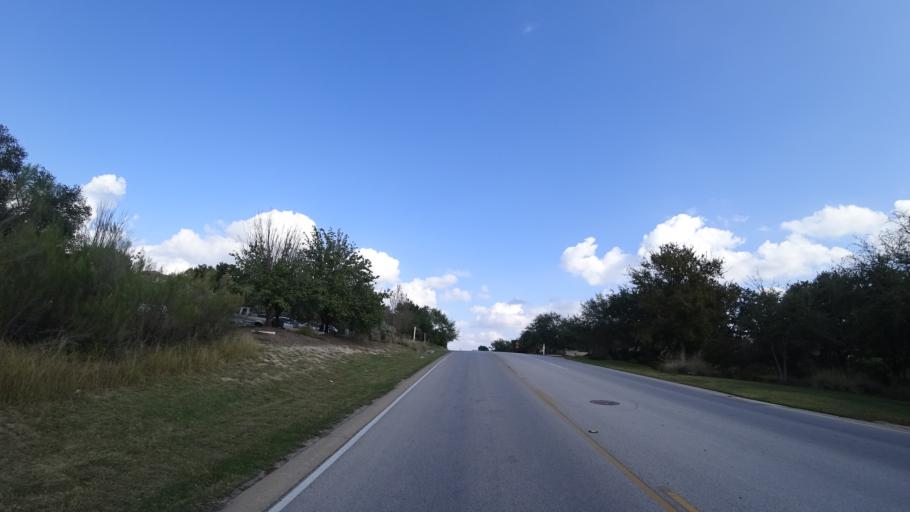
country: US
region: Texas
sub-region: Travis County
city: Barton Creek
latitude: 30.2895
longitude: -97.8664
